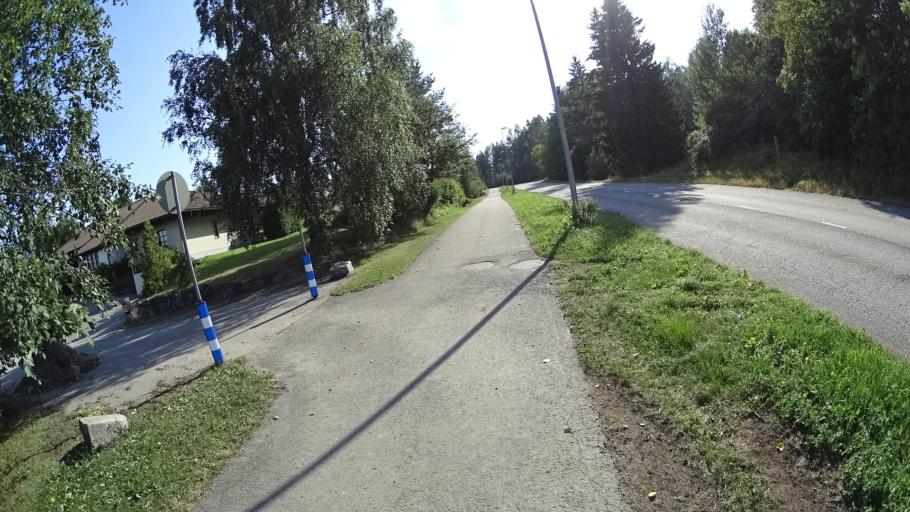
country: FI
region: Uusimaa
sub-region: Porvoo
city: Porvoo
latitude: 60.4126
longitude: 25.6522
